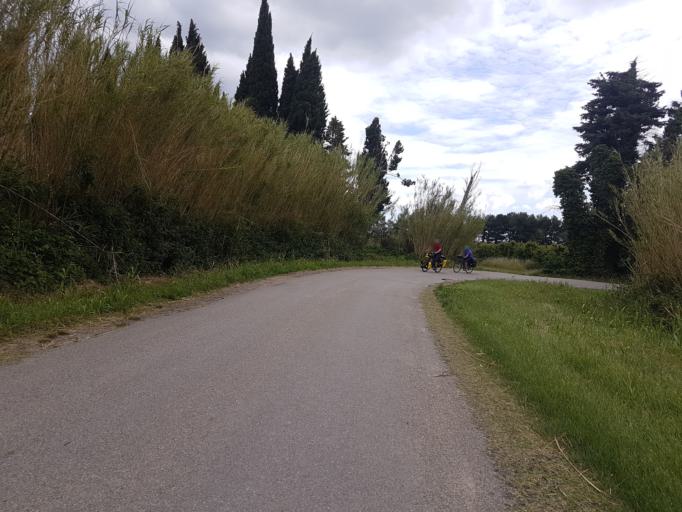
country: FR
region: Languedoc-Roussillon
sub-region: Departement du Gard
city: Vallabregues
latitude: 43.8707
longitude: 4.6228
